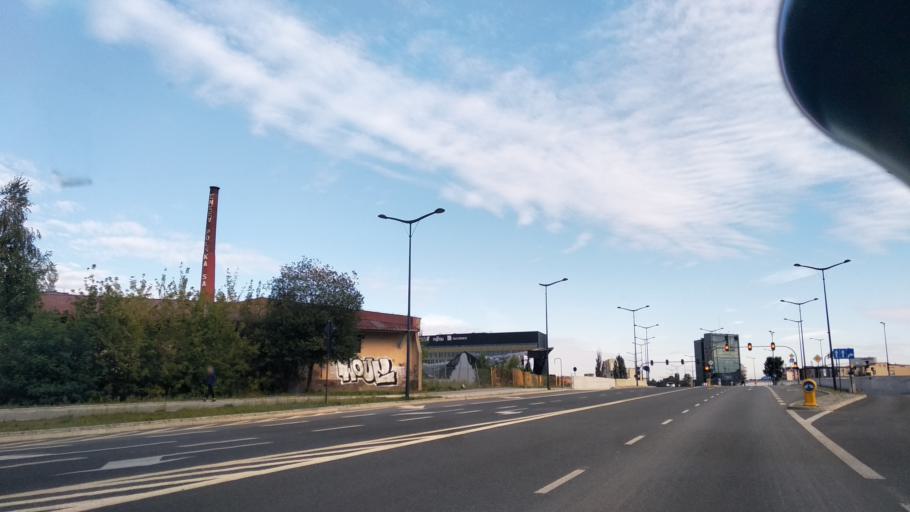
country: PL
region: Lodz Voivodeship
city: Lodz
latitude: 51.7672
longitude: 19.4733
